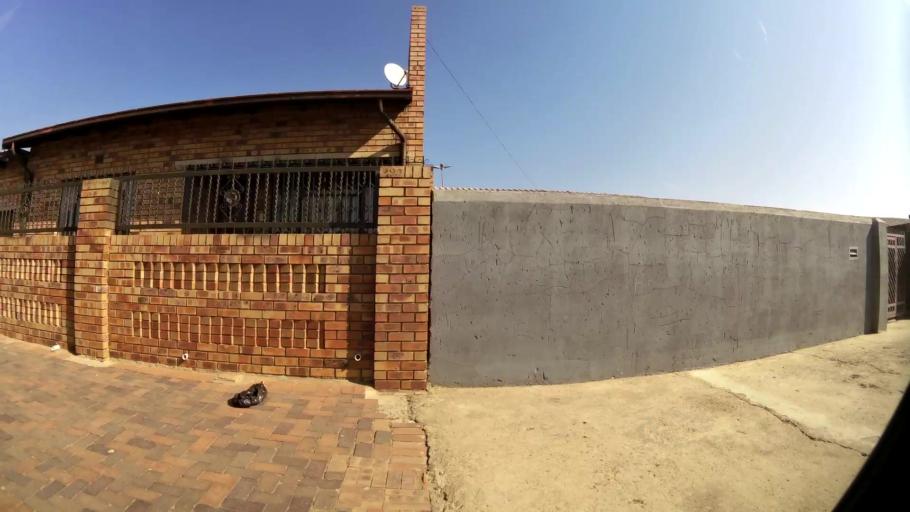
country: ZA
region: Gauteng
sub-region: City of Johannesburg Metropolitan Municipality
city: Soweto
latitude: -26.2444
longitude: 27.9532
